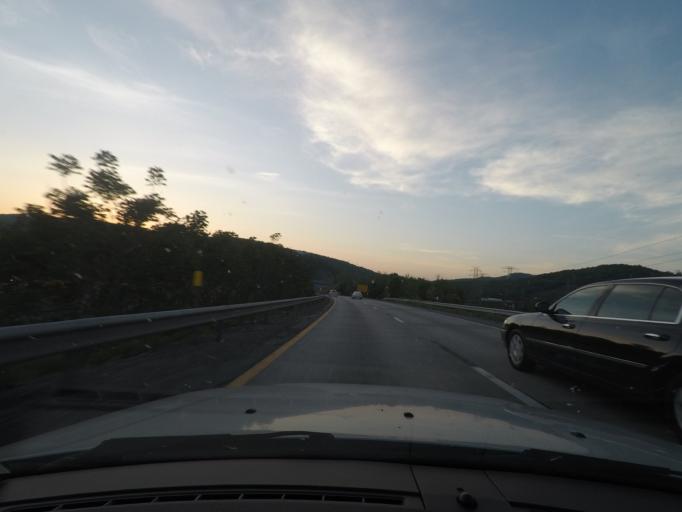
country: US
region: New York
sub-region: Rockland County
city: Suffern
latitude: 41.1221
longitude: -74.1627
